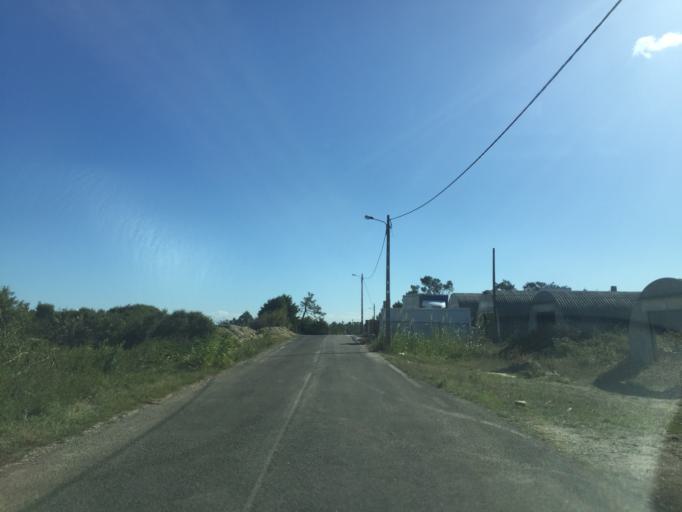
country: PT
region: Coimbra
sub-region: Figueira da Foz
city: Tavarede
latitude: 40.1951
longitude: -8.8475
